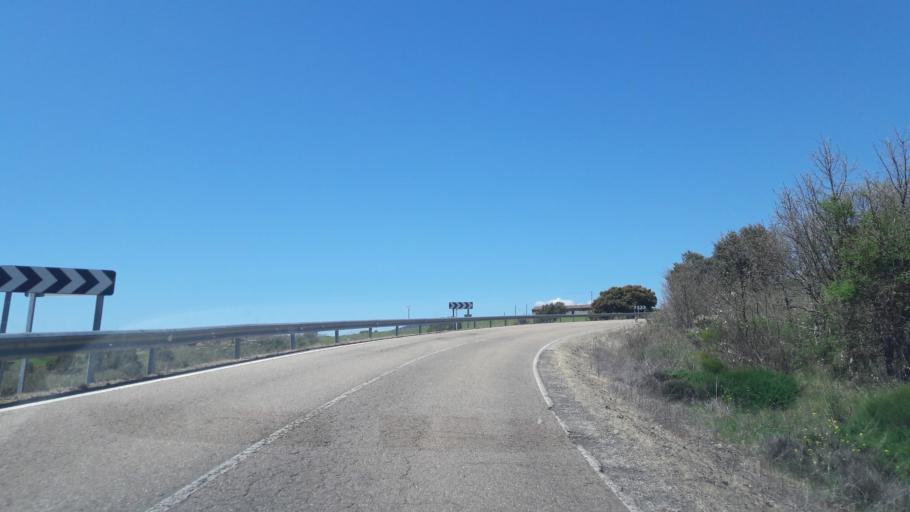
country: ES
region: Castille and Leon
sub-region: Provincia de Salamanca
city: Monleon
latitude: 40.5891
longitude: -5.8371
